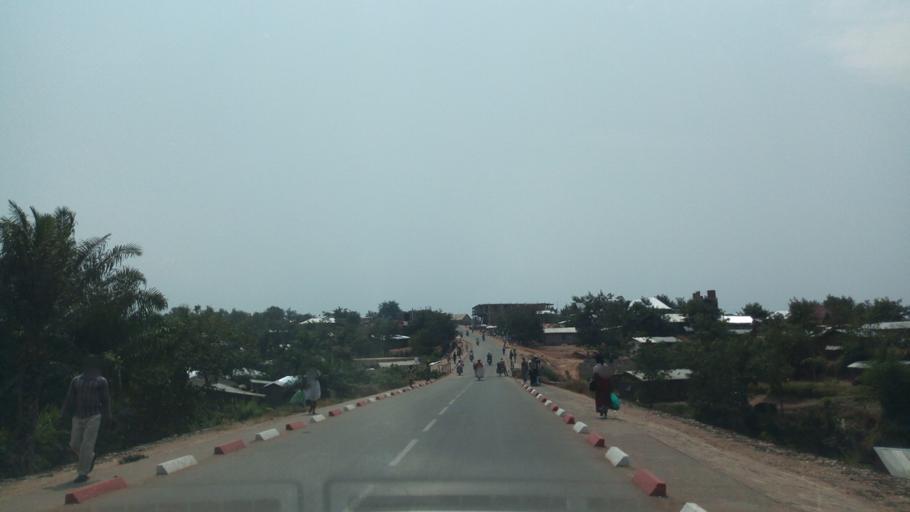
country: CD
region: Katanga
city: Kalemie
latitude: -5.9023
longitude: 29.2009
